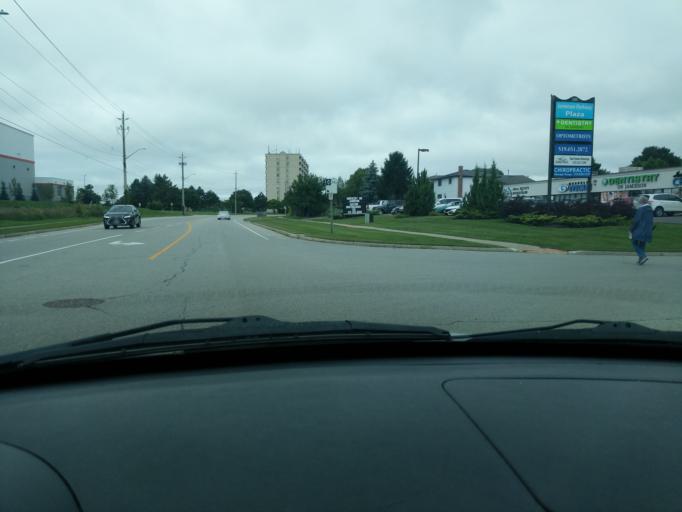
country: CA
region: Ontario
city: Cambridge
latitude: 43.4175
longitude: -80.3029
